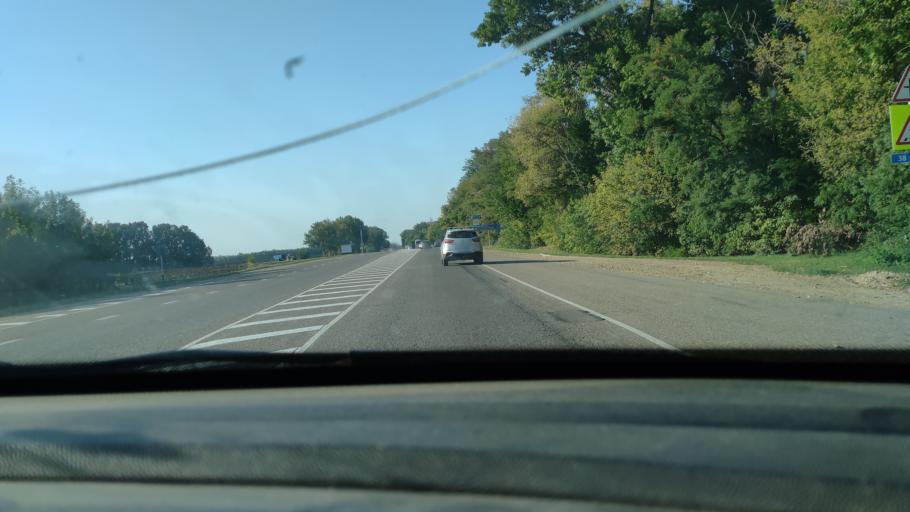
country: RU
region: Krasnodarskiy
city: Medvedovskaya
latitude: 45.4506
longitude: 38.9915
